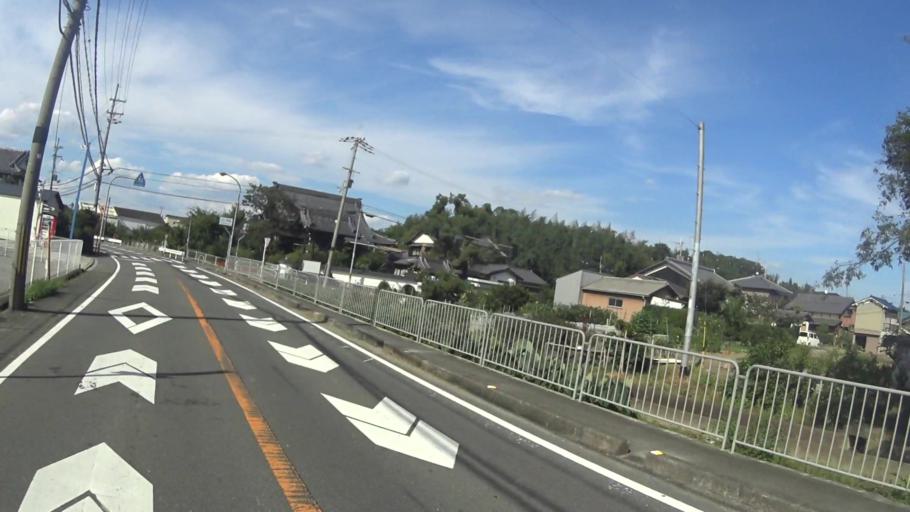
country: JP
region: Kyoto
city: Yawata
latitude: 34.8639
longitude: 135.7455
